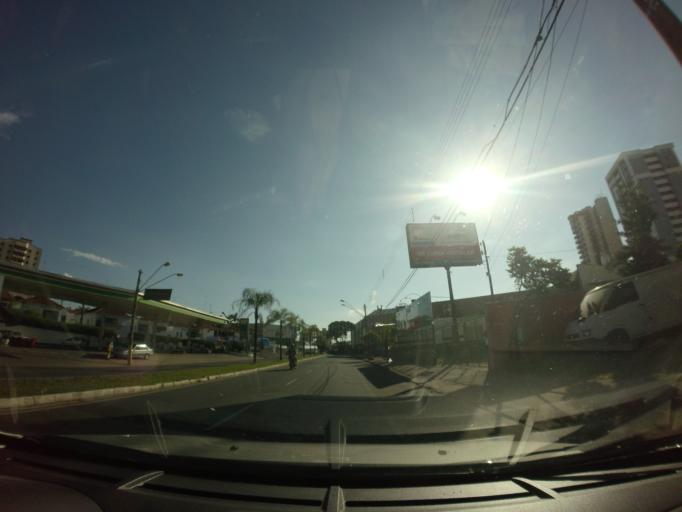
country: BR
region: Sao Paulo
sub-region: Rio Claro
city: Rio Claro
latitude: -22.4121
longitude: -47.5686
